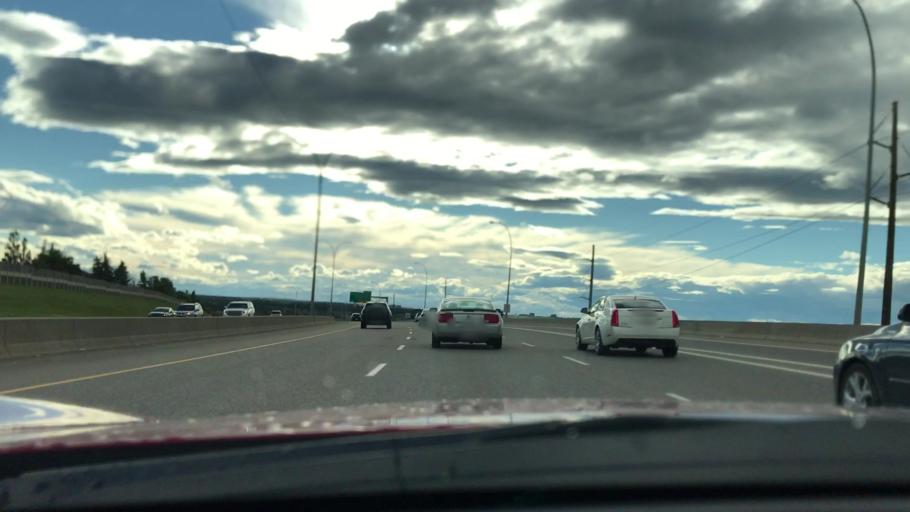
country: CA
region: Alberta
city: Calgary
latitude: 50.9463
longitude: -113.9864
